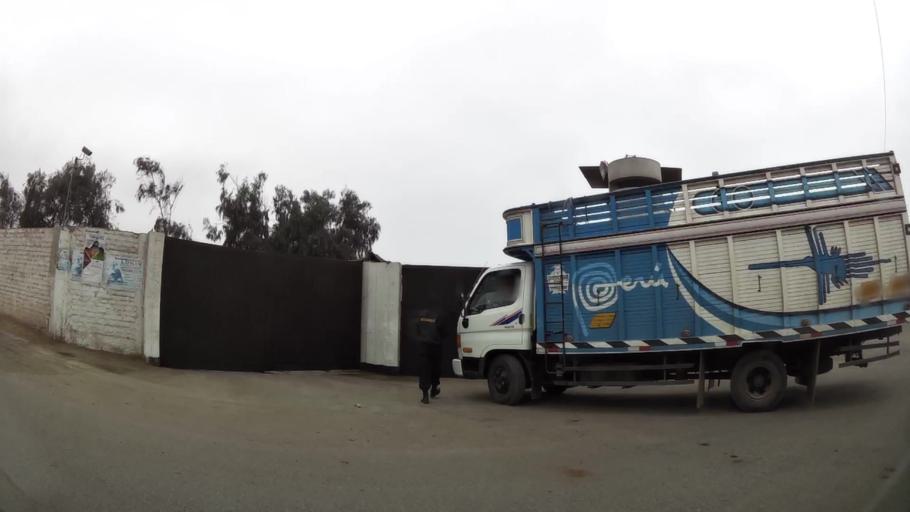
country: PE
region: Lima
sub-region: Lima
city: Punta Hermosa
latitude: -12.3005
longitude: -76.8443
